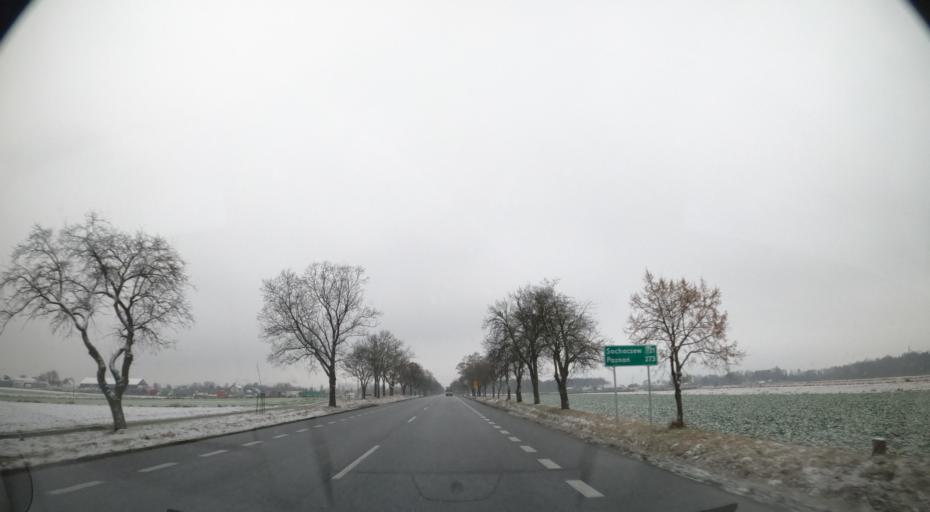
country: PL
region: Masovian Voivodeship
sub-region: Powiat warszawski zachodni
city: Bieniewice
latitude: 52.2023
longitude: 20.5350
